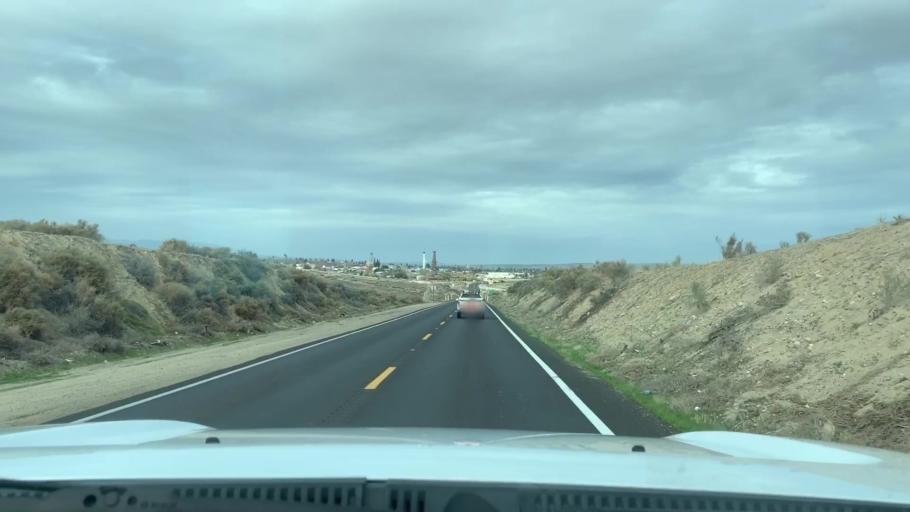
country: US
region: California
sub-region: Kern County
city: South Taft
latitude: 35.1270
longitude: -119.4411
